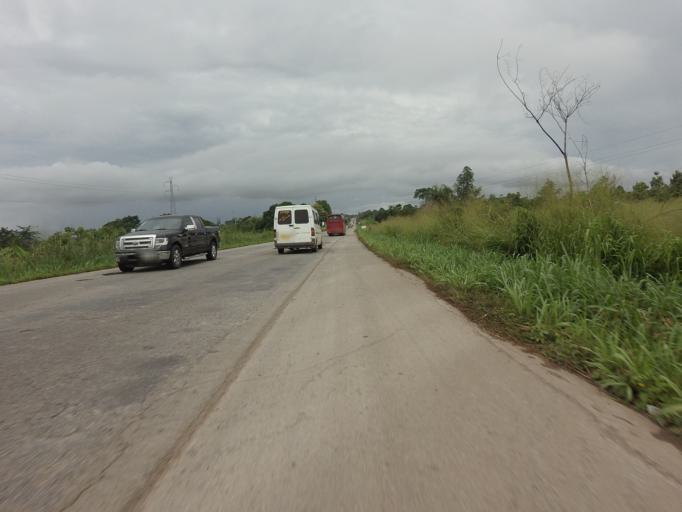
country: GH
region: Ashanti
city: Konongo
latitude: 6.5985
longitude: -1.1353
